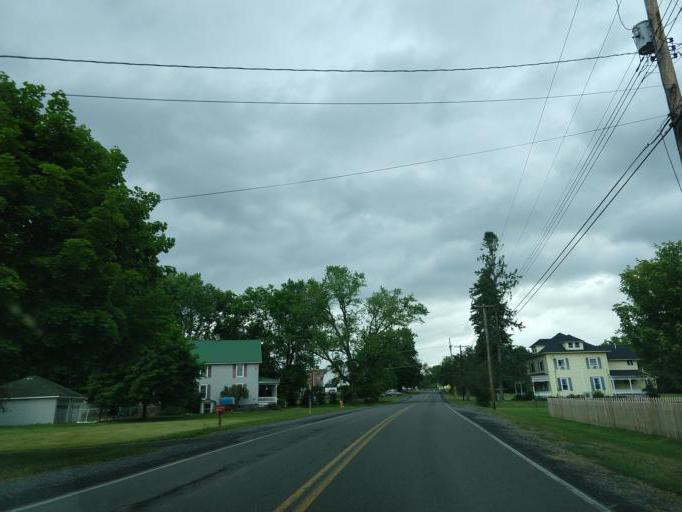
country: US
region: New York
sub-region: Tompkins County
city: Northwest Ithaca
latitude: 42.5407
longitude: -76.5388
